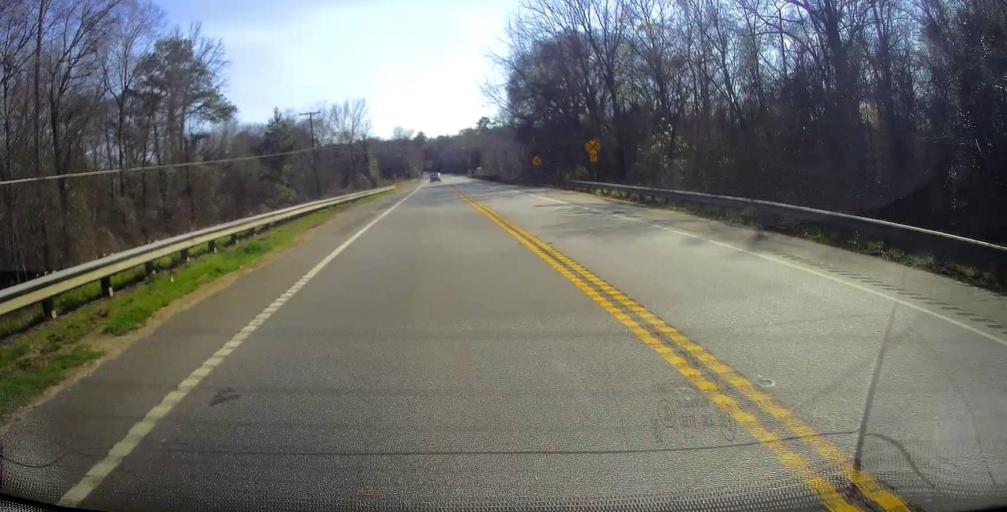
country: US
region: Georgia
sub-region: Macon County
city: Oglethorpe
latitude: 32.3124
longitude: -84.0649
